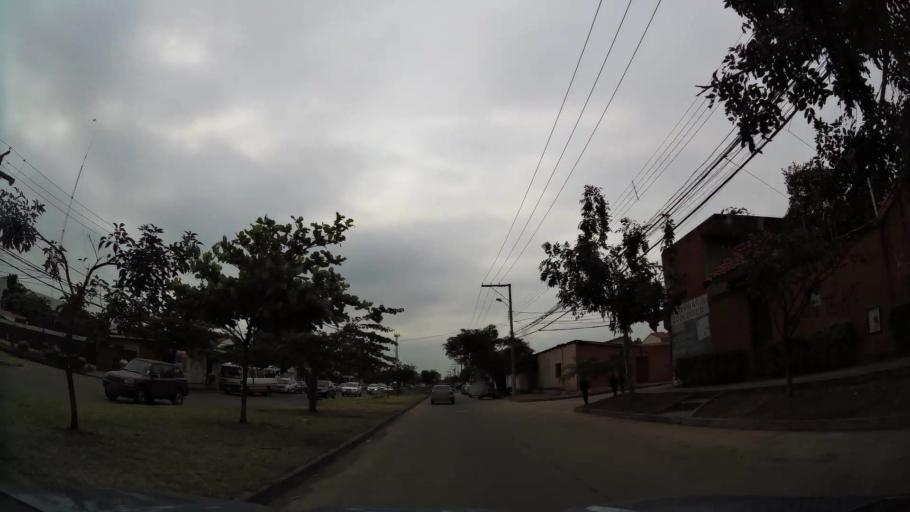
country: BO
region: Santa Cruz
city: Santa Cruz de la Sierra
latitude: -17.7566
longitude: -63.1820
